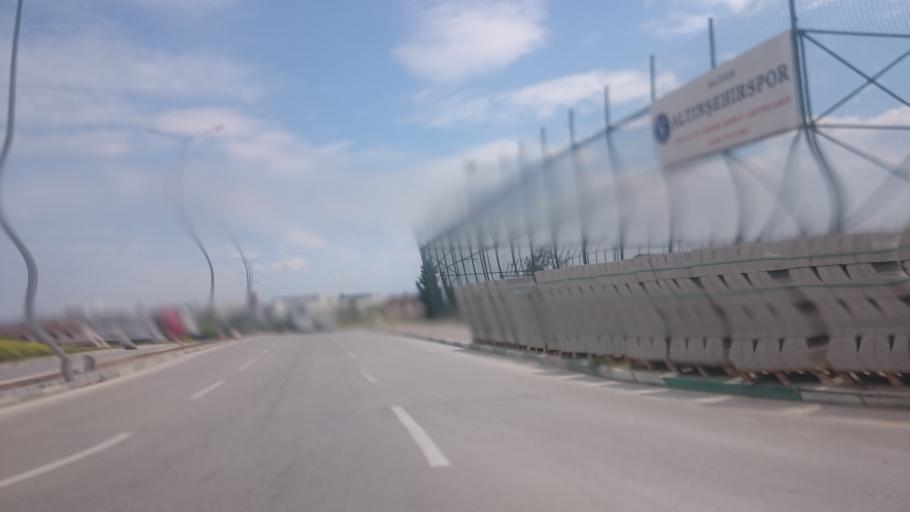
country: TR
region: Bursa
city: Niluefer
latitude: 40.2348
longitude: 28.9204
